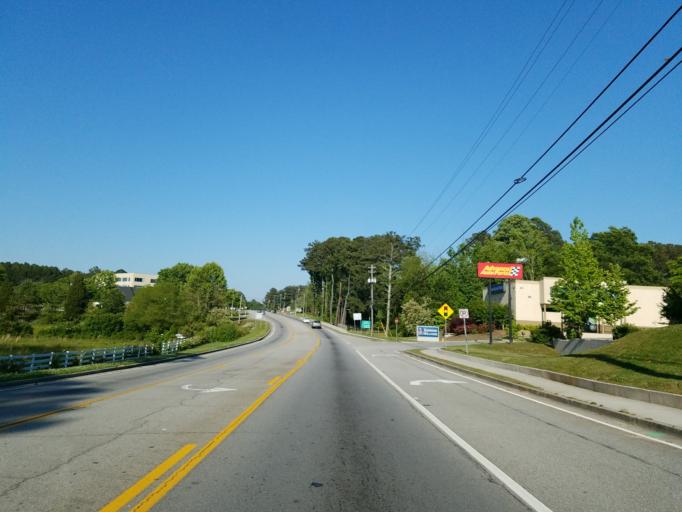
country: US
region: Georgia
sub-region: Carroll County
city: Villa Rica
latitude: 33.7308
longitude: -84.9345
